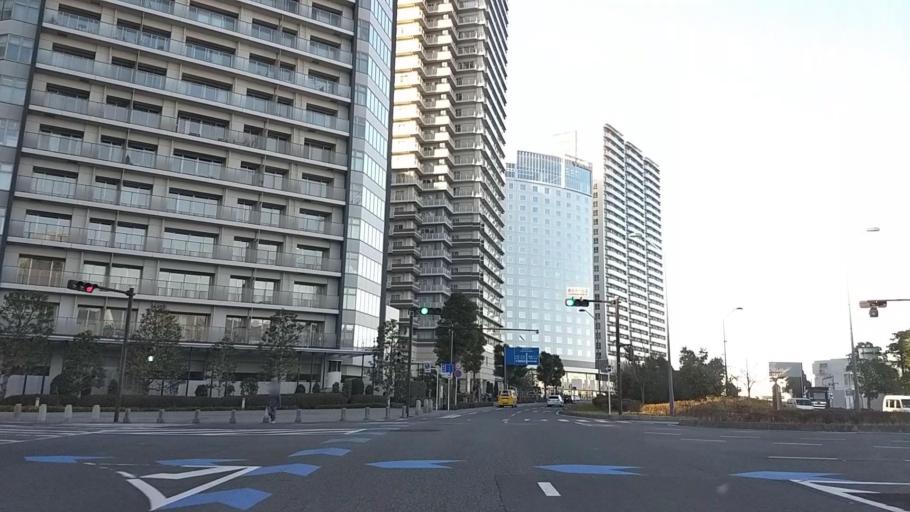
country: JP
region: Kanagawa
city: Yokohama
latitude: 35.4611
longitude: 139.6330
